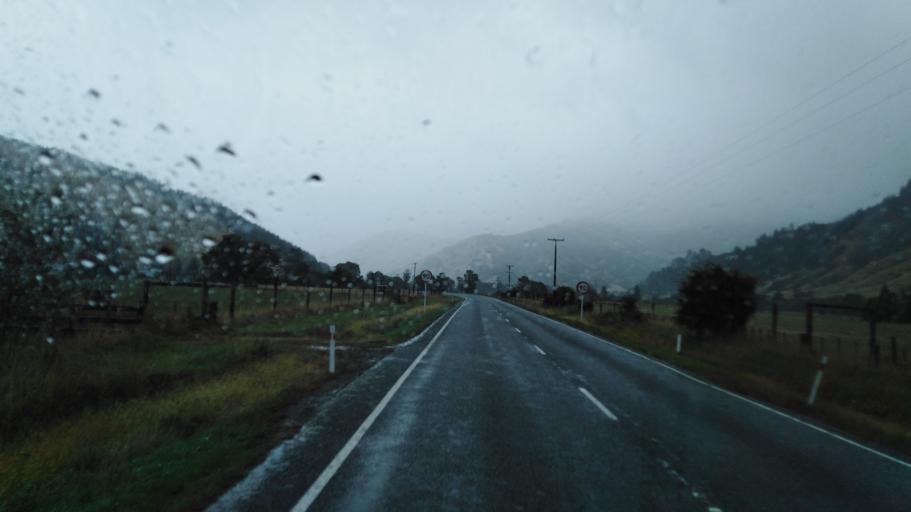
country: NZ
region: Marlborough
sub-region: Marlborough District
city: Blenheim
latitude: -41.3508
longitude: 173.7645
